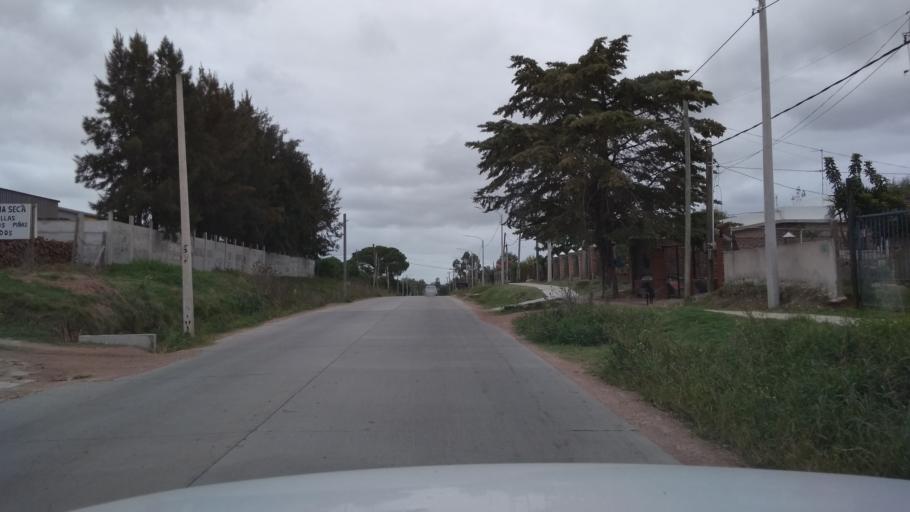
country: UY
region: Canelones
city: Toledo
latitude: -34.7874
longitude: -56.1428
